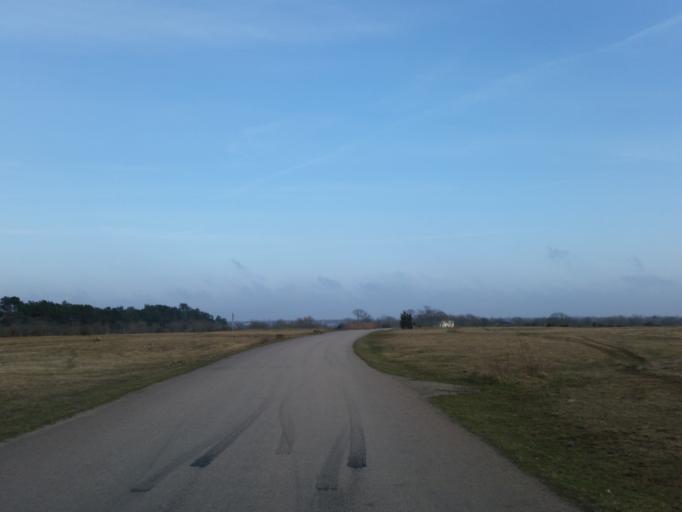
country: SE
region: Kalmar
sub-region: Borgholms Kommun
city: Borgholm
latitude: 56.8692
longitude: 16.6501
